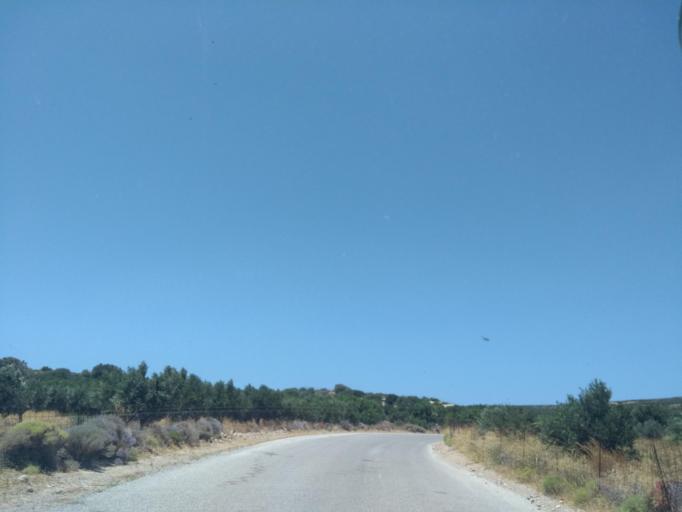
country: GR
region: Crete
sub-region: Nomos Chanias
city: Vryses
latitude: 35.3369
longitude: 23.5452
